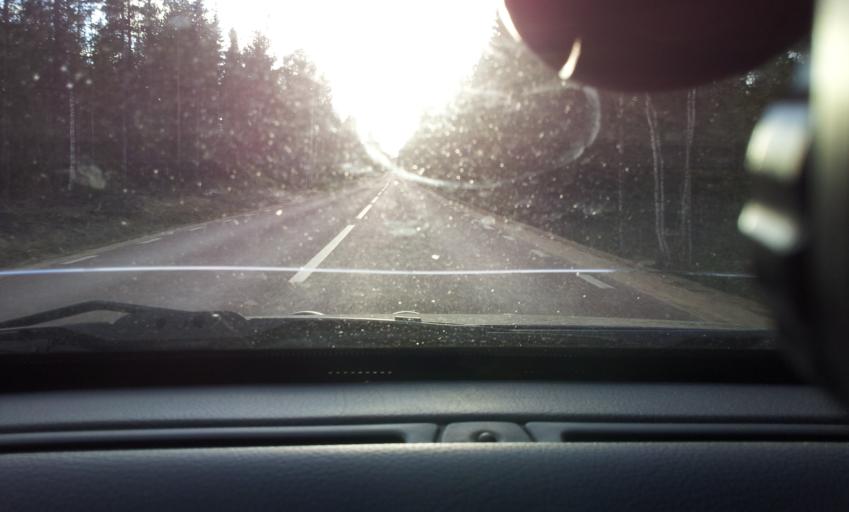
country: SE
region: Jaemtland
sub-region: Harjedalens Kommun
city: Sveg
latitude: 62.1789
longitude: 14.9002
